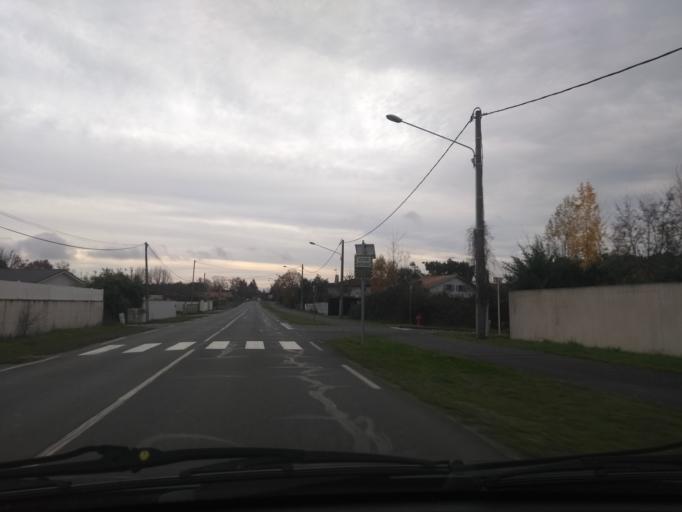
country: FR
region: Aquitaine
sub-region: Departement de la Gironde
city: Leognan
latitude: 44.7396
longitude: -0.6172
